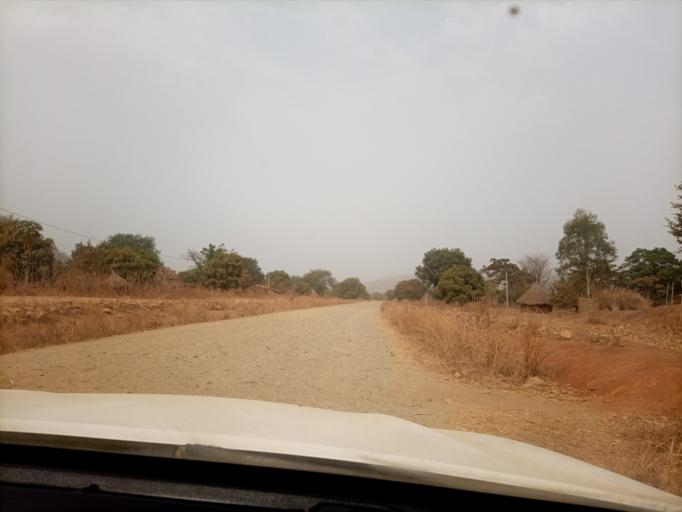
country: ET
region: Oromiya
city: Mendi
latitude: 10.1671
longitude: 35.0976
